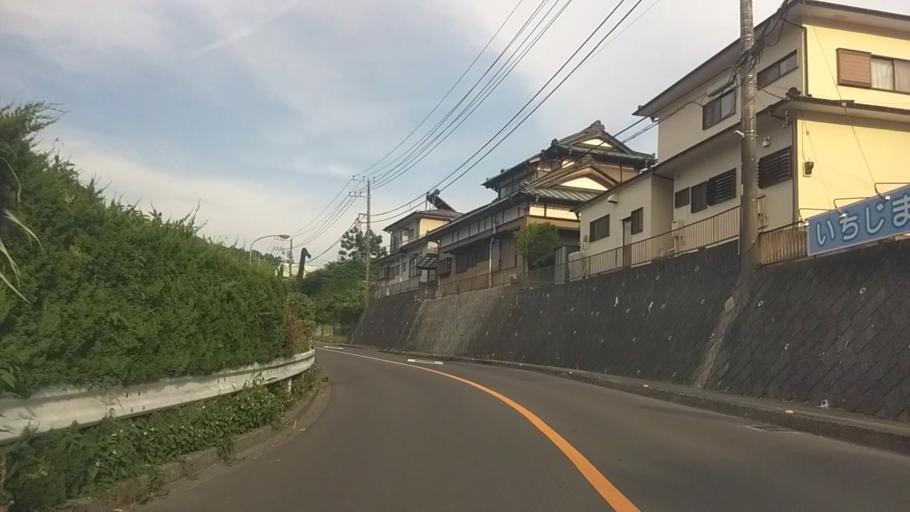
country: JP
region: Kanagawa
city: Odawara
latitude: 35.3608
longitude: 139.0845
